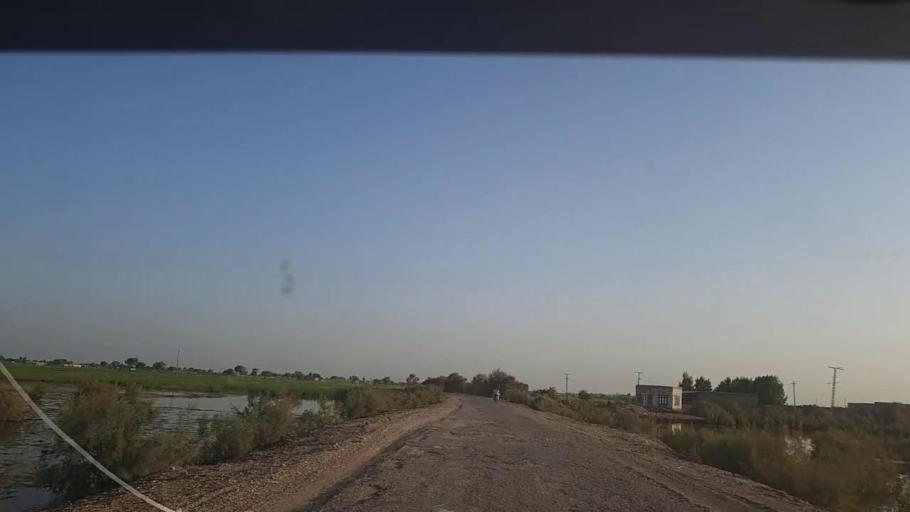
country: PK
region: Sindh
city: Thul
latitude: 28.1393
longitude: 68.8870
